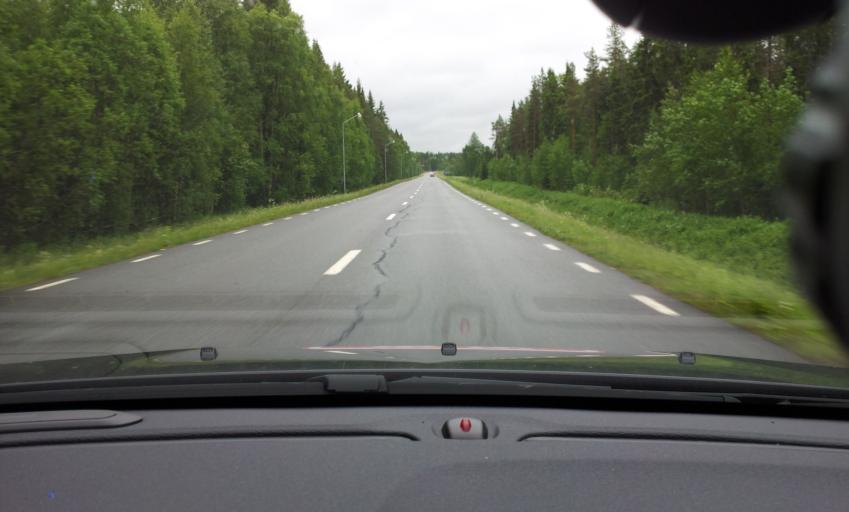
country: SE
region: Jaemtland
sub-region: Stroemsunds Kommun
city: Stroemsund
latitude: 63.5406
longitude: 15.4316
